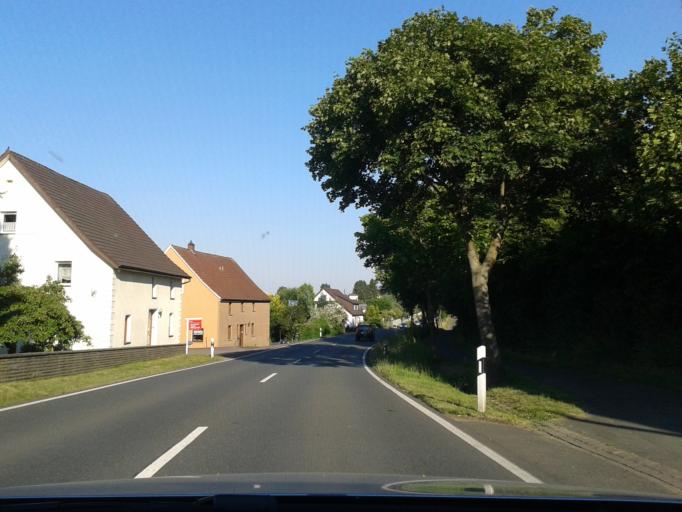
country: DE
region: North Rhine-Westphalia
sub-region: Regierungsbezirk Detmold
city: Dorentrup
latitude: 52.0279
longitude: 9.0415
